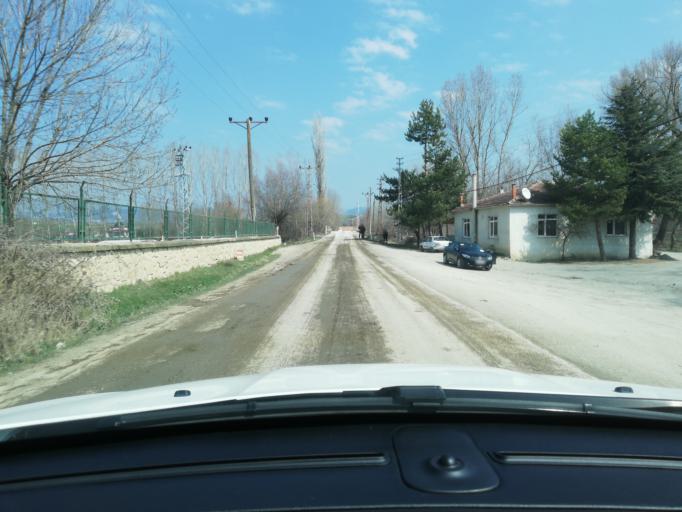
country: TR
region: Kastamonu
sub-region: Cide
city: Kastamonu
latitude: 41.4527
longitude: 33.7667
